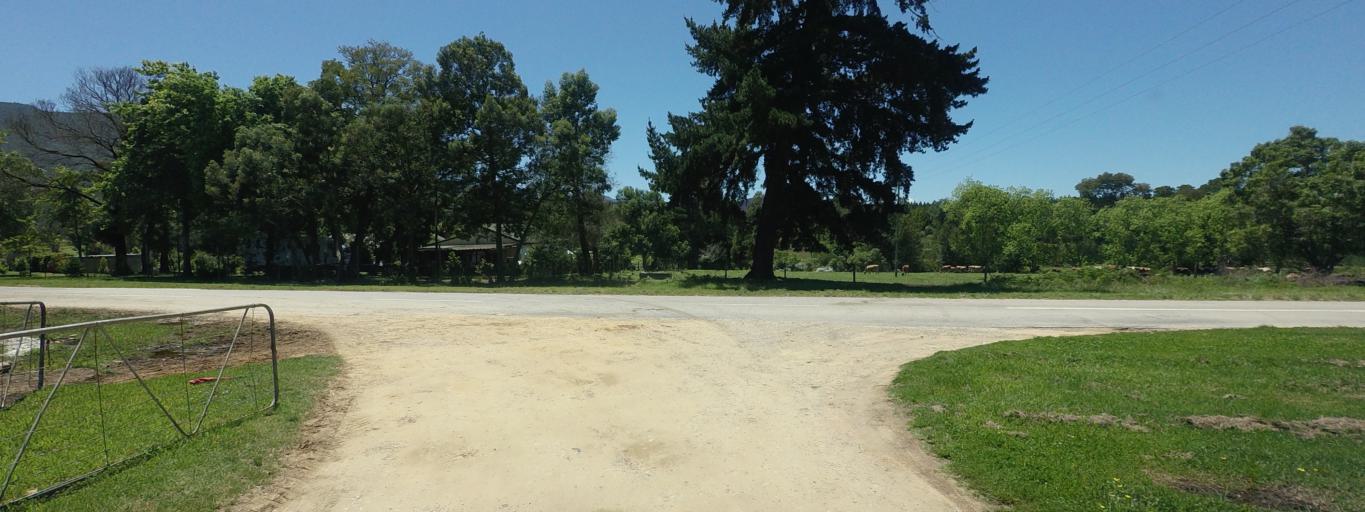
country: ZA
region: Western Cape
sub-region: Eden District Municipality
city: Plettenberg Bay
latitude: -33.9434
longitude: 23.5115
